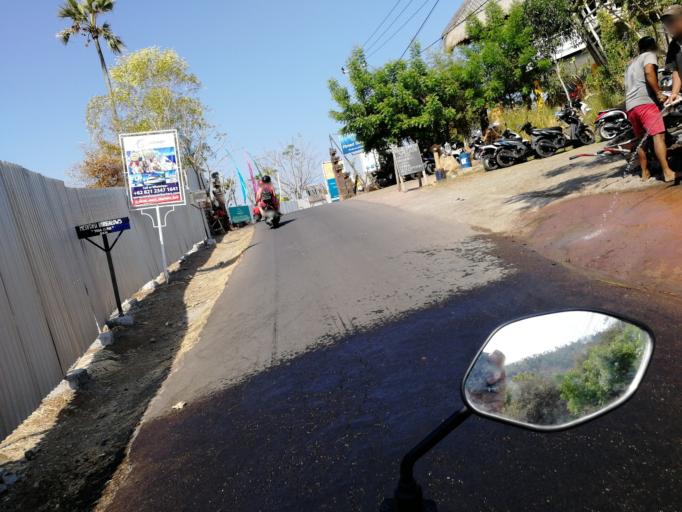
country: ID
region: Bali
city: Biaslantang Kaler
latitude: -8.3384
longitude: 115.6623
